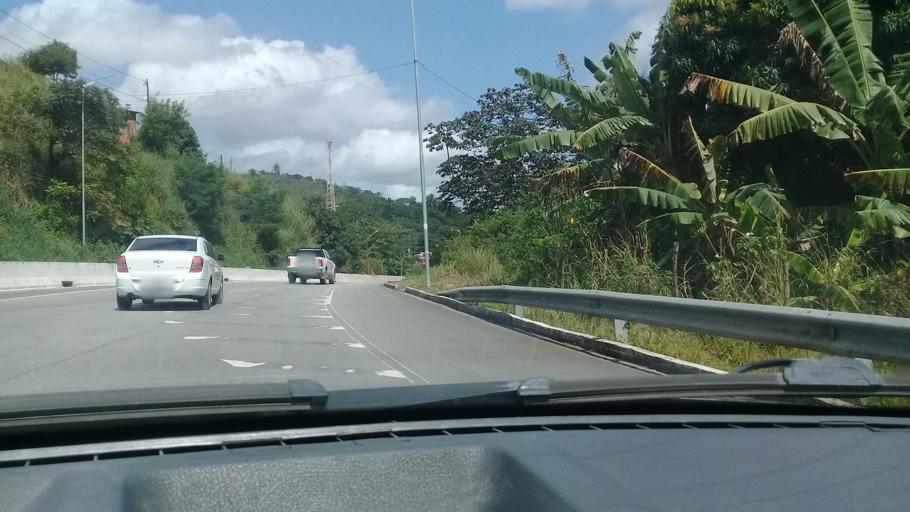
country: BR
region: Pernambuco
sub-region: Jaboatao Dos Guararapes
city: Jaboatao dos Guararapes
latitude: -8.0823
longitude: -34.9927
